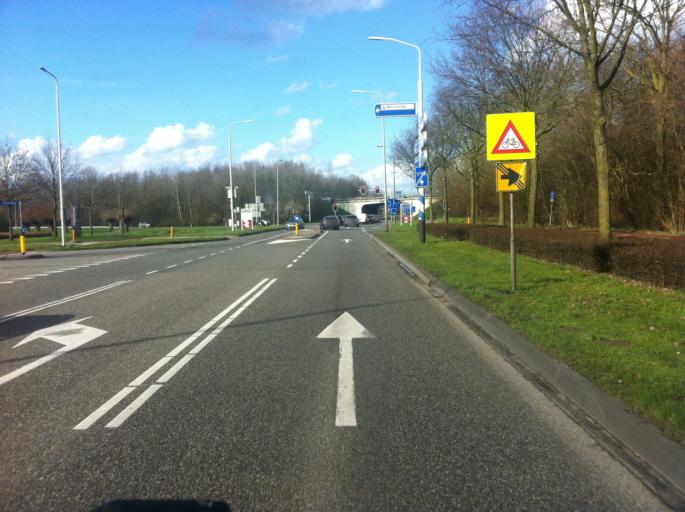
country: NL
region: Gelderland
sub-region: Gemeente Zevenaar
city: Zevenaar
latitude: 51.9406
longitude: 6.0821
